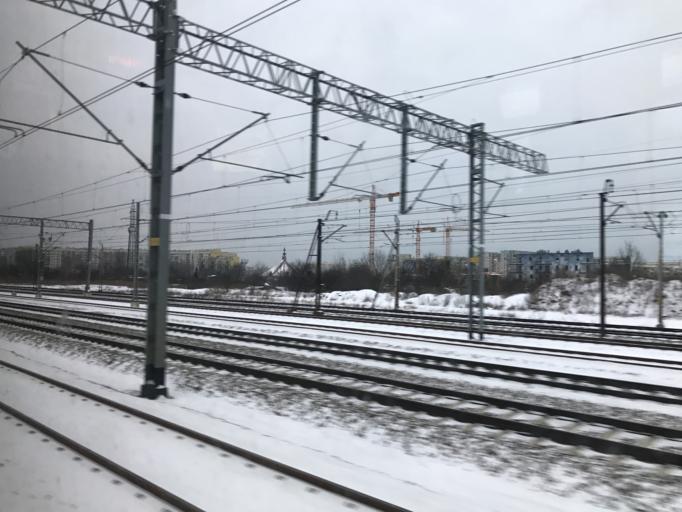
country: PL
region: Pomeranian Voivodeship
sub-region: Gdansk
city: Gdansk
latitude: 54.3862
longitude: 18.5977
